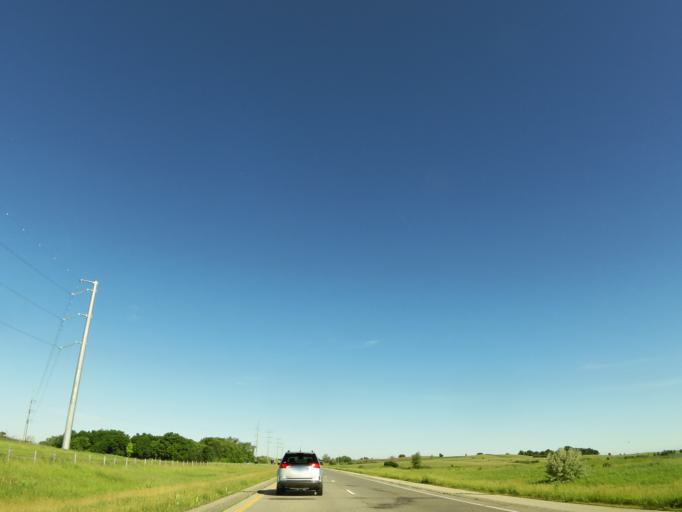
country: US
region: Minnesota
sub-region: Grant County
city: Elbow Lake
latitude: 46.0153
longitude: -95.7834
